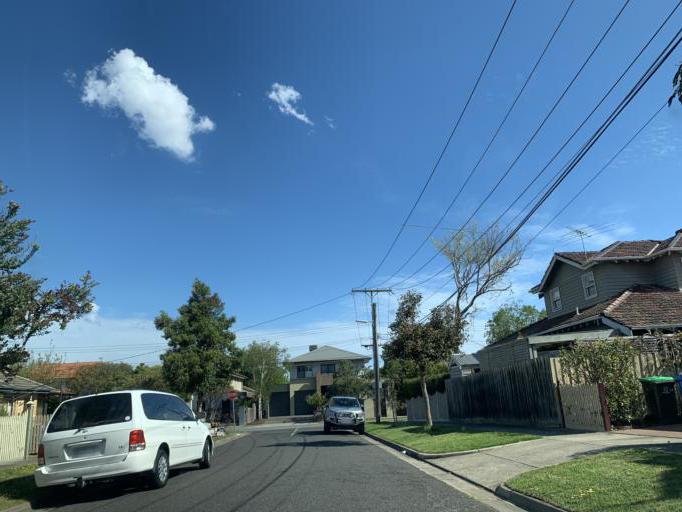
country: AU
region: Victoria
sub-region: Bayside
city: Hampton East
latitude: -37.9401
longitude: 145.0202
